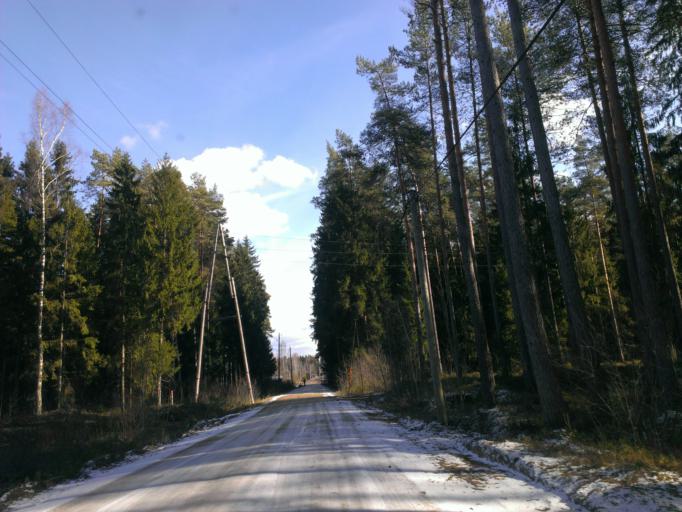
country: LV
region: Garkalne
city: Garkalne
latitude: 56.9510
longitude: 24.4462
